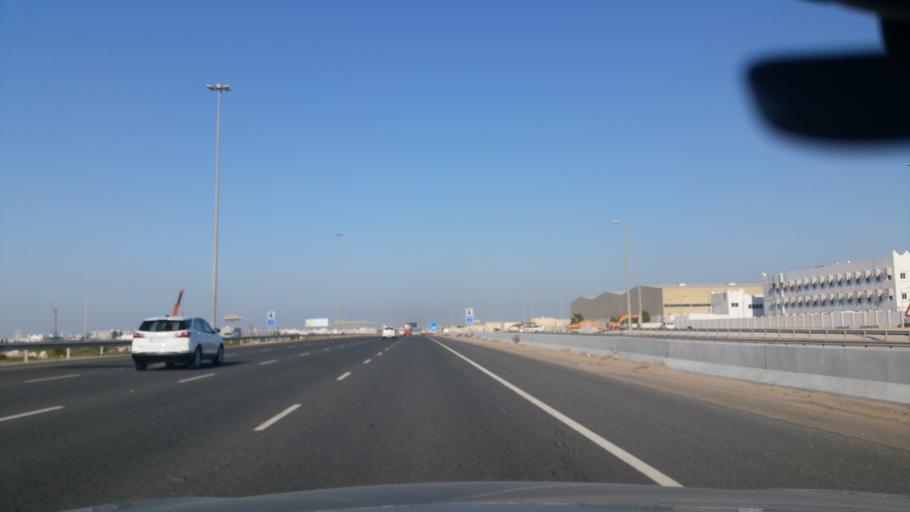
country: QA
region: Baladiyat ar Rayyan
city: Ar Rayyan
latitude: 25.2124
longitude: 51.4097
